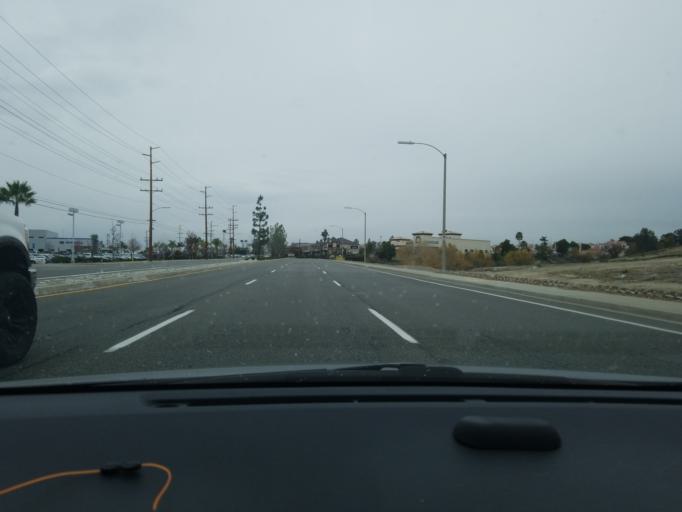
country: US
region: California
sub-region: Riverside County
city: Temecula
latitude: 33.5085
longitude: -117.1505
